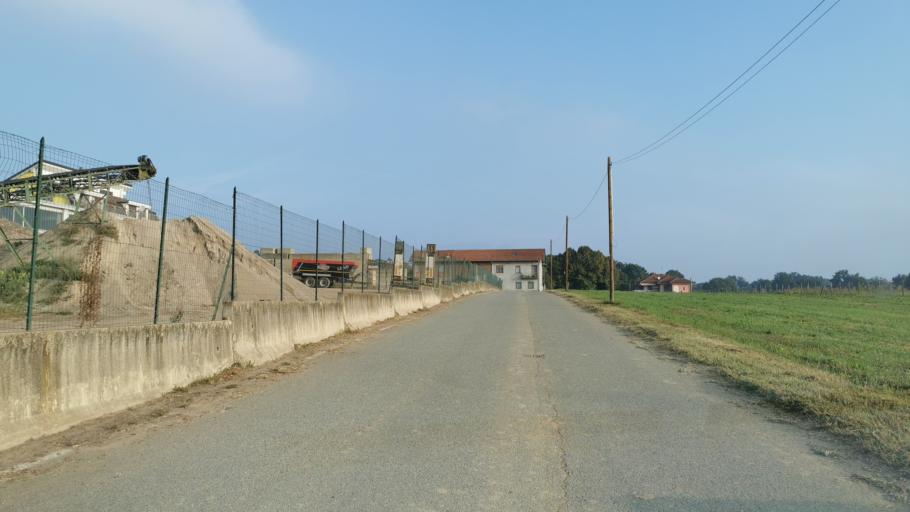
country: IT
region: Piedmont
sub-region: Provincia di Torino
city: Front
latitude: 45.2573
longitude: 7.6623
